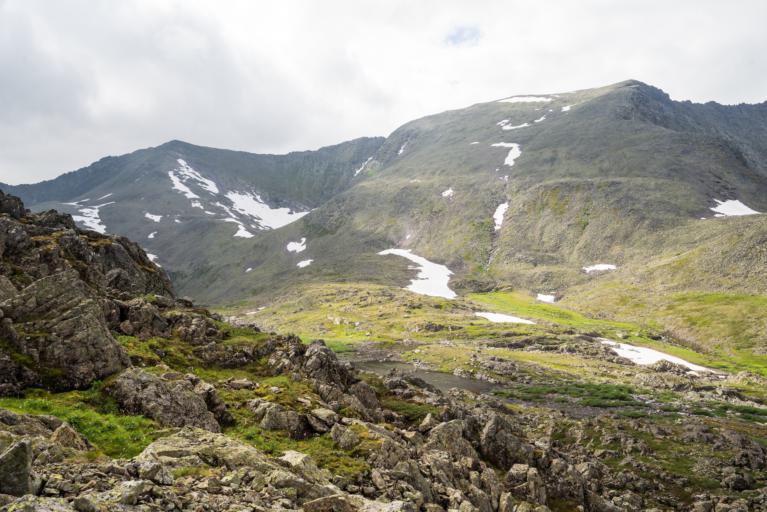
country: RU
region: Komi Republic
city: Synya
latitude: 64.8239
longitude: 59.2577
